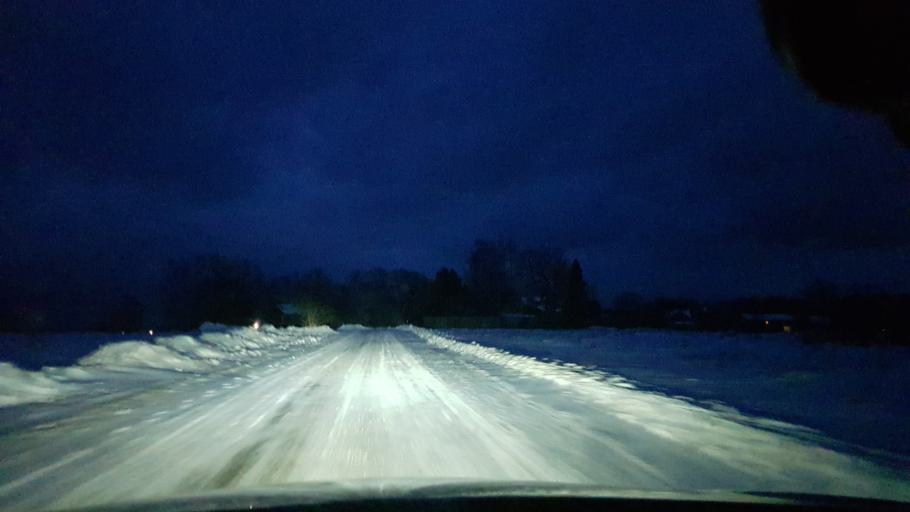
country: EE
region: Laeaene
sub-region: Haapsalu linn
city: Haapsalu
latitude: 59.2201
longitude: 23.5249
